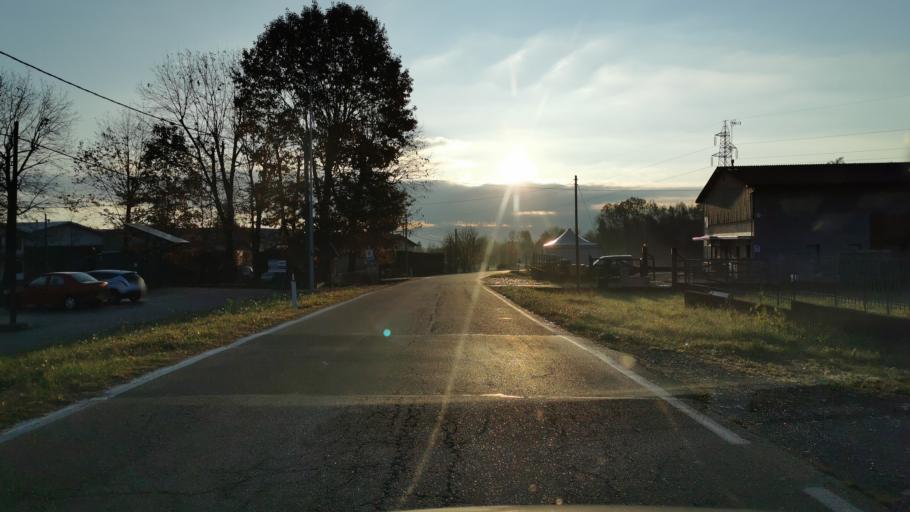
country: IT
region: Piedmont
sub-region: Provincia di Torino
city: Rocca Canavese
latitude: 45.3058
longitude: 7.5823
